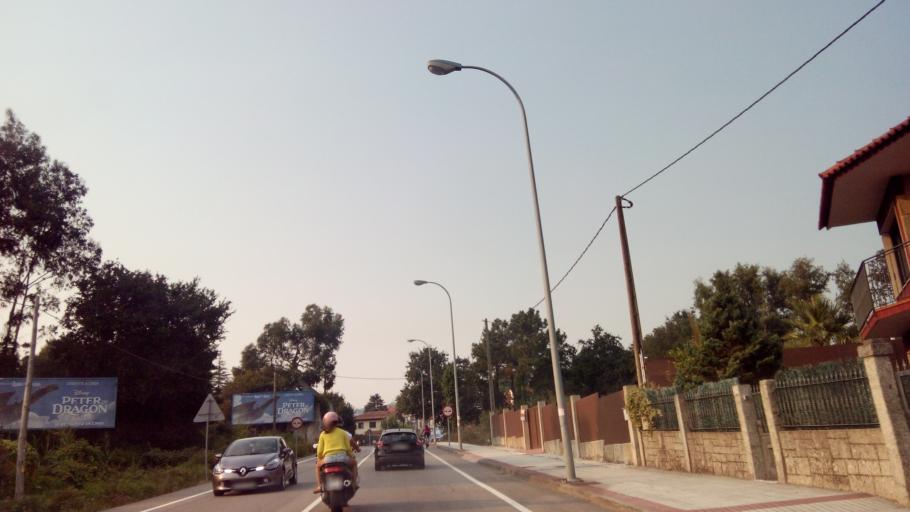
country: ES
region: Galicia
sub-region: Provincia de Pontevedra
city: Nigran
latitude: 42.1355
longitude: -8.8081
